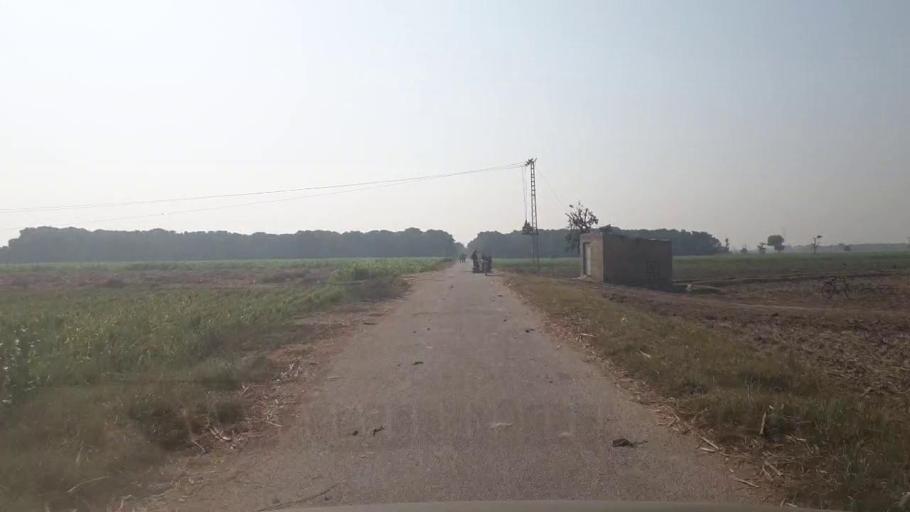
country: PK
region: Sindh
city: Tando Allahyar
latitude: 25.4738
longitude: 68.7619
